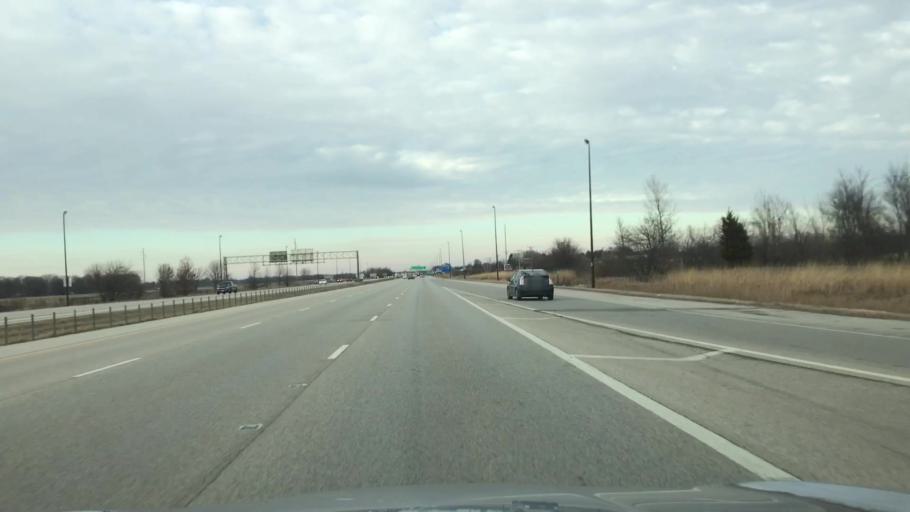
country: US
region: Illinois
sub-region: Sangamon County
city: Southern View
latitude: 39.7166
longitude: -89.6437
